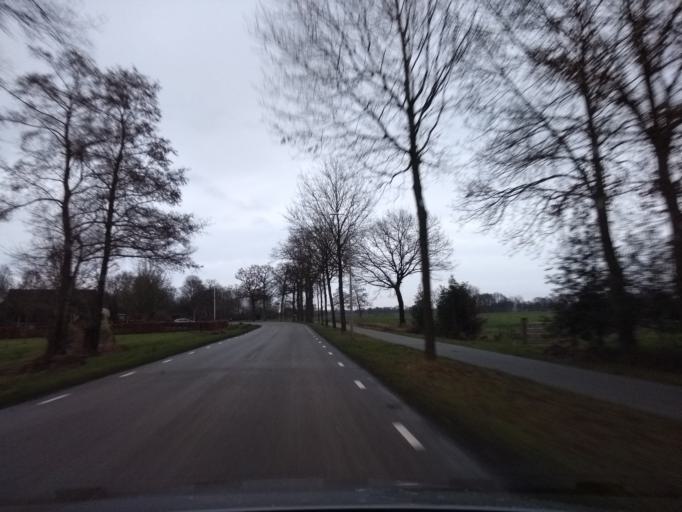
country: NL
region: Overijssel
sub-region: Gemeente Staphorst
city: Staphorst
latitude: 52.6713
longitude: 6.3083
